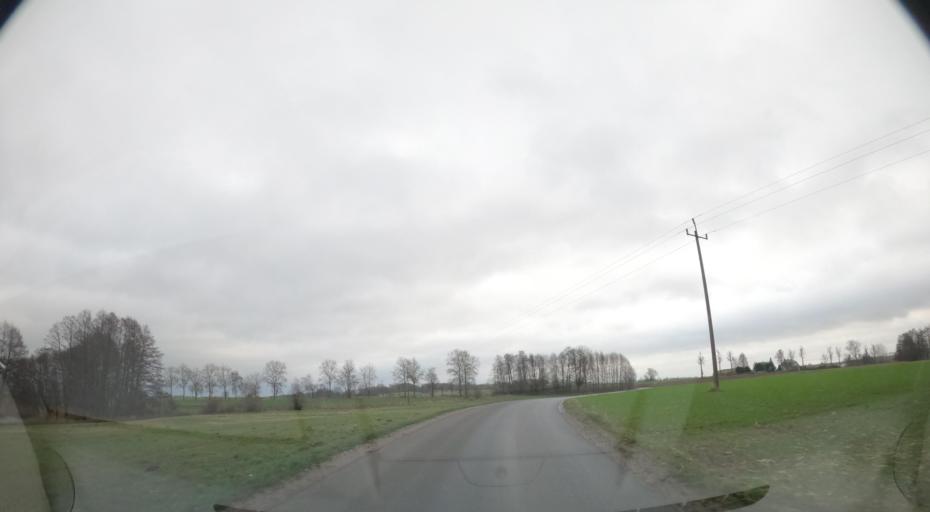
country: PL
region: Greater Poland Voivodeship
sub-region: Powiat pilski
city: Wysoka
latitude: 53.2527
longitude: 17.1468
